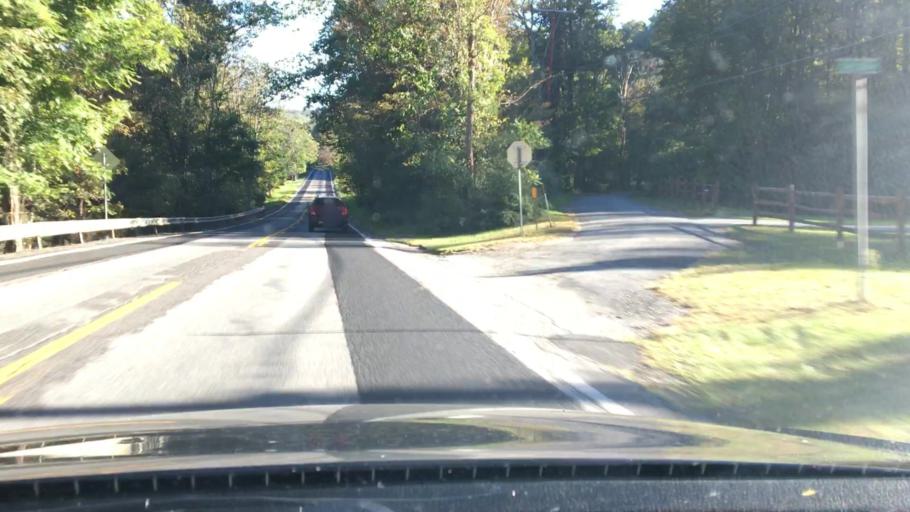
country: US
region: Connecticut
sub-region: Fairfield County
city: Sherman
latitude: 41.6511
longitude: -73.5299
